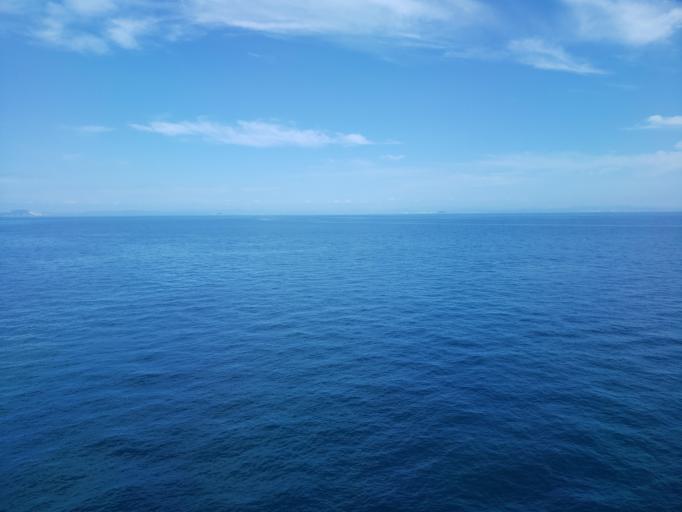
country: JP
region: Hyogo
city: Shirahamacho-usazakiminami
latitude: 34.5501
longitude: 134.7344
